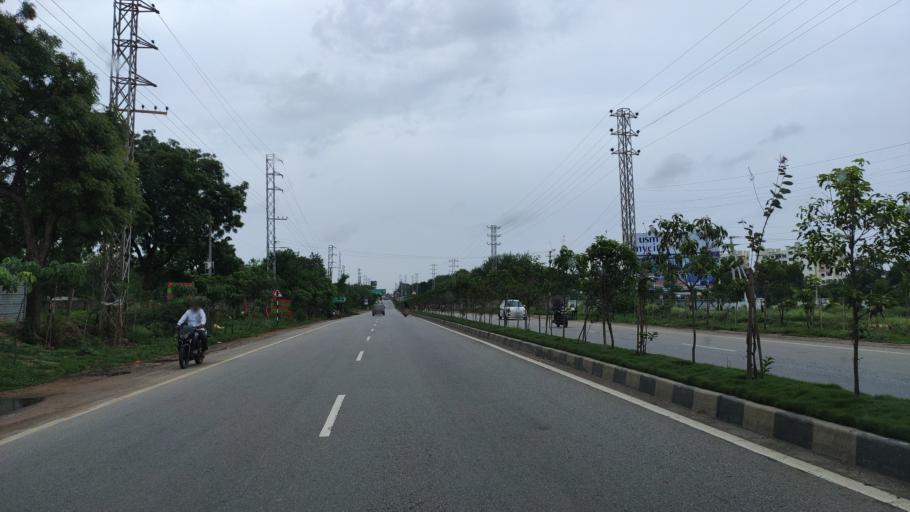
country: IN
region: Telangana
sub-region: Rangareddi
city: Secunderabad
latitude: 17.5852
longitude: 78.5735
